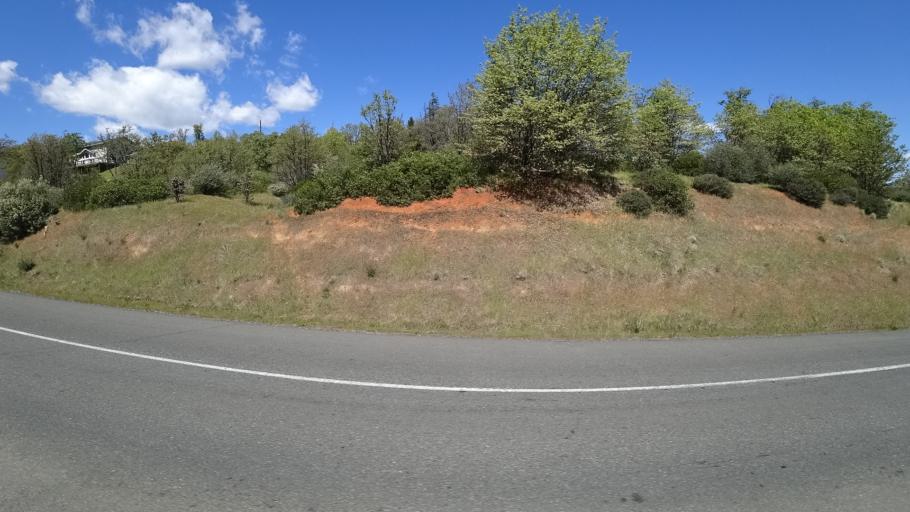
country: US
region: California
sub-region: Trinity County
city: Weaverville
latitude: 40.7361
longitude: -122.9636
